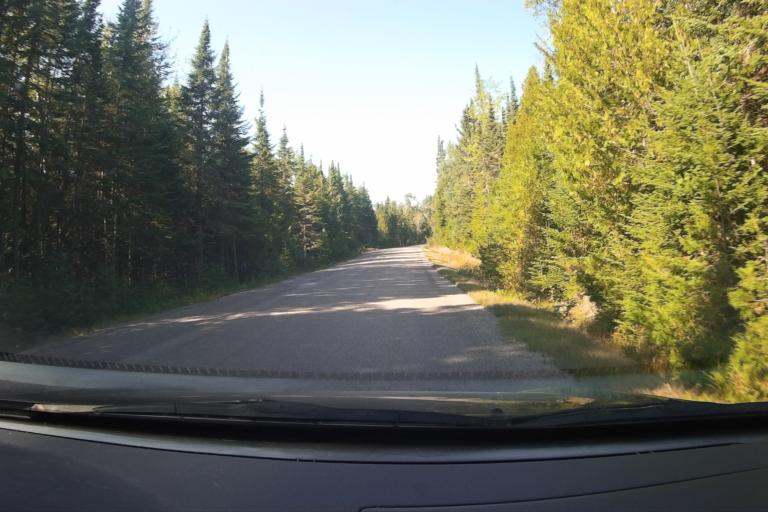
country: CA
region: Ontario
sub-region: Thunder Bay District
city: Thunder Bay
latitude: 48.3444
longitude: -88.8125
